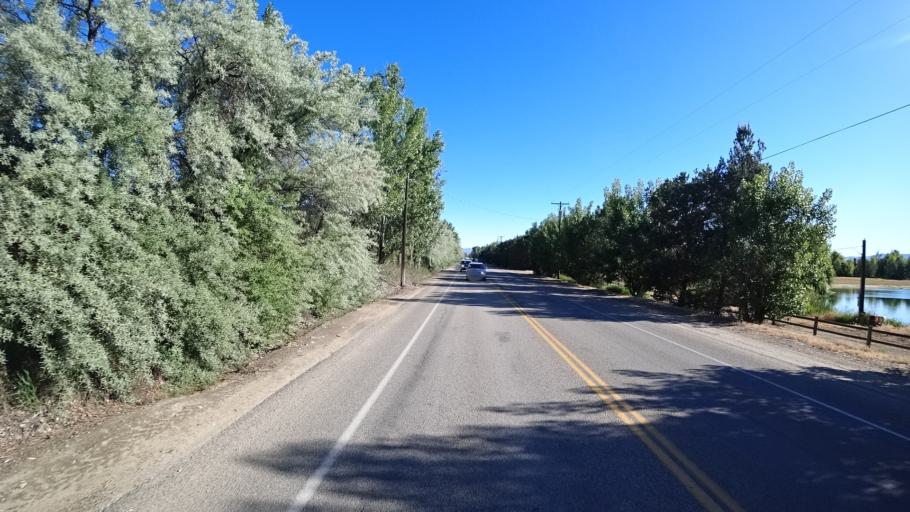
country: US
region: Idaho
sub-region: Ada County
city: Eagle
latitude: 43.6743
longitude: -116.4137
